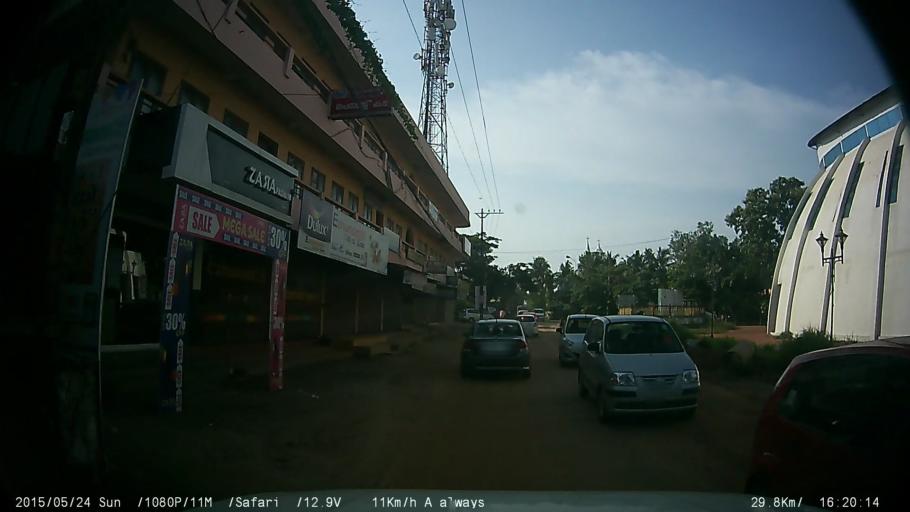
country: IN
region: Kerala
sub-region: Alappuzha
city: Alleppey
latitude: 9.4940
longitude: 76.3289
